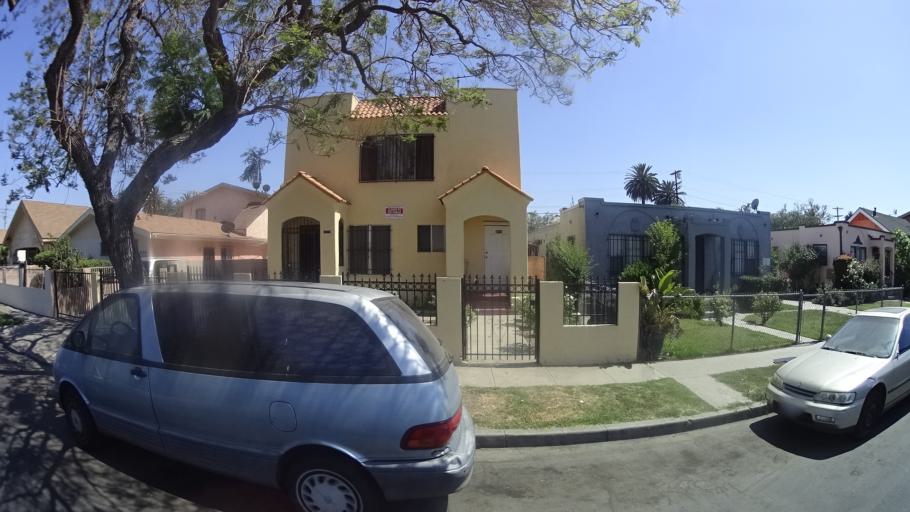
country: US
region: California
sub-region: Los Angeles County
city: View Park-Windsor Hills
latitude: 34.0173
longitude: -118.3106
